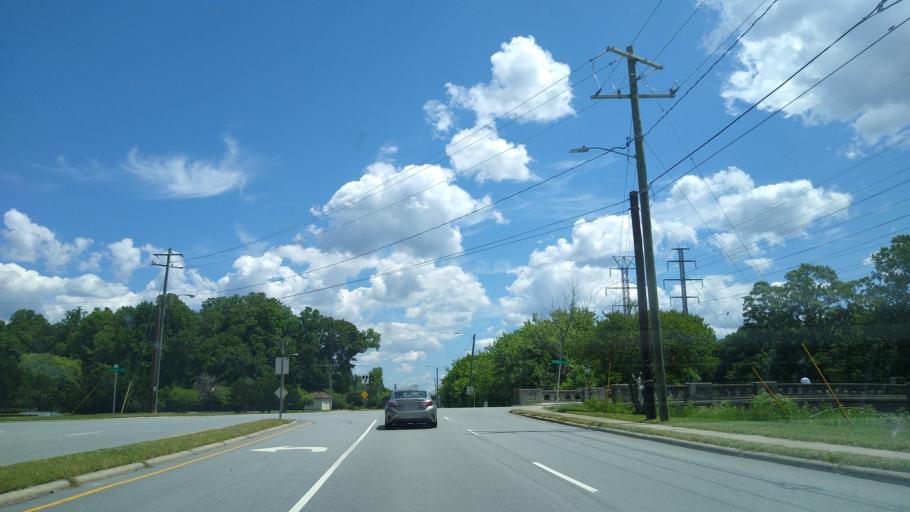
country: US
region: North Carolina
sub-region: Guilford County
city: Greensboro
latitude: 36.0794
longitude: -79.8085
